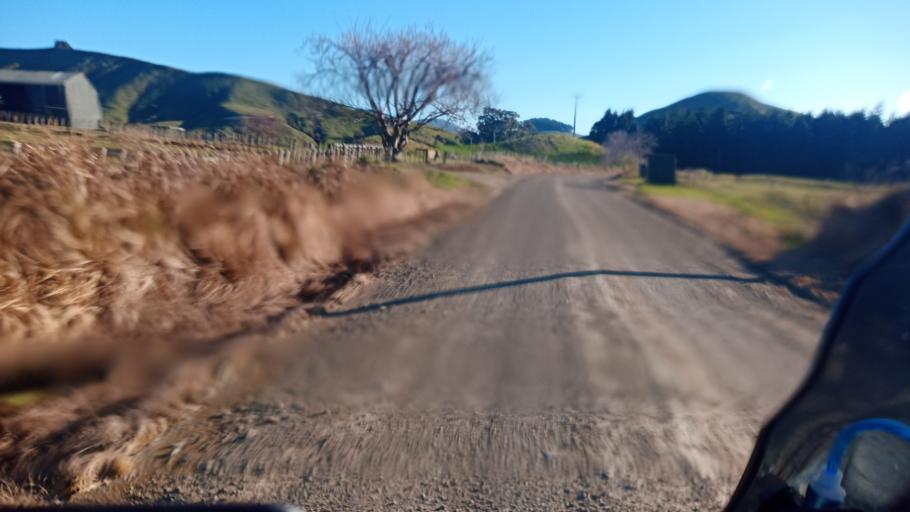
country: NZ
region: Bay of Plenty
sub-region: Opotiki District
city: Opotiki
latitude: -38.4591
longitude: 177.4286
